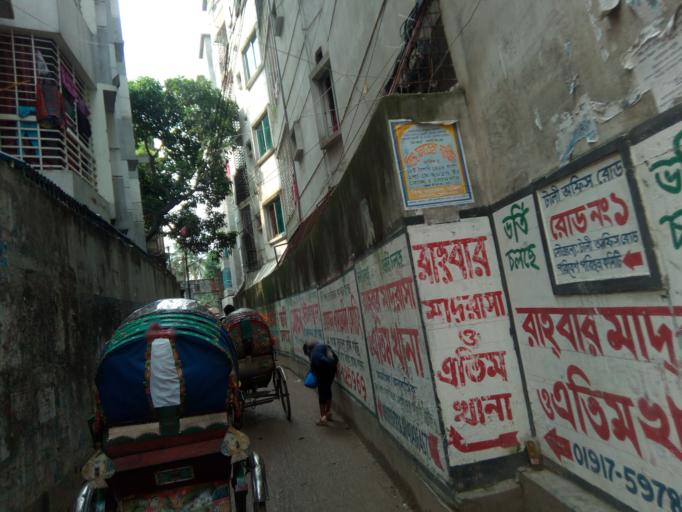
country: BD
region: Dhaka
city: Azimpur
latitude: 23.7411
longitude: 90.3656
